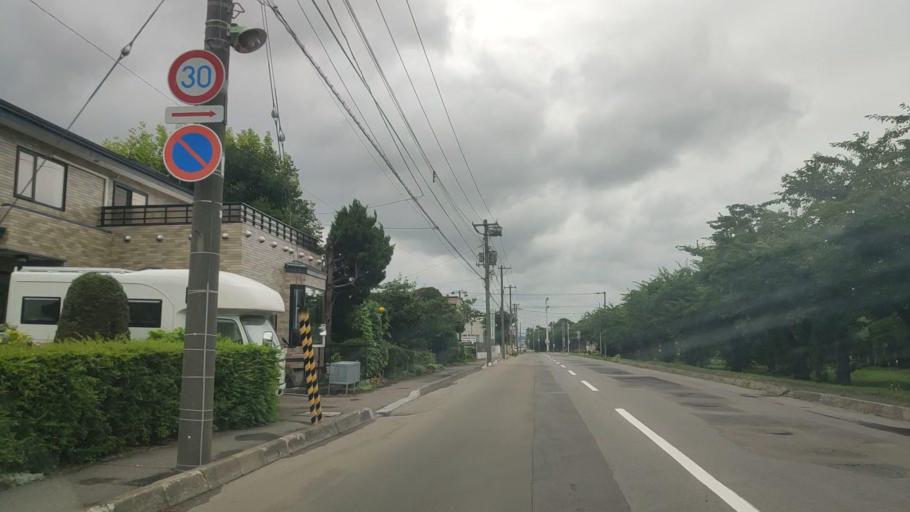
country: JP
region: Hokkaido
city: Hakodate
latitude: 41.7992
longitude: 140.7551
